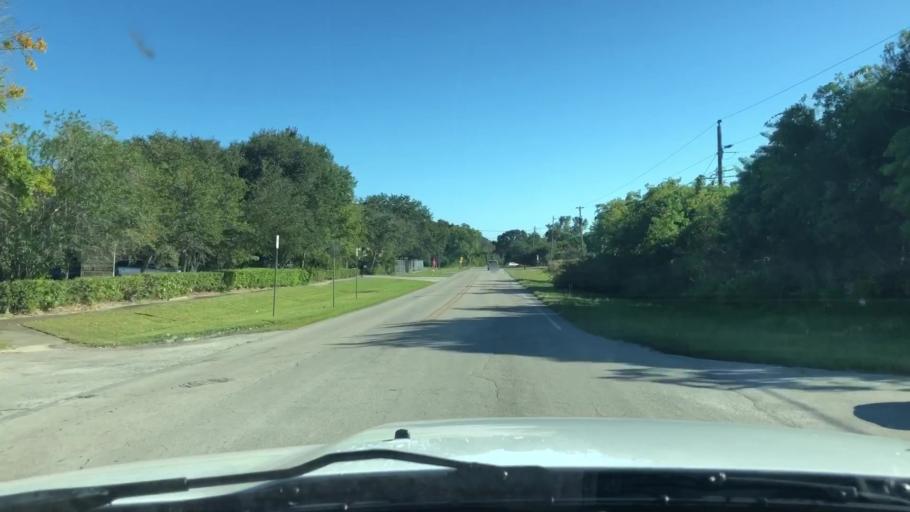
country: US
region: Florida
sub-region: Indian River County
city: Florida Ridge
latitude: 27.5780
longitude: -80.3772
